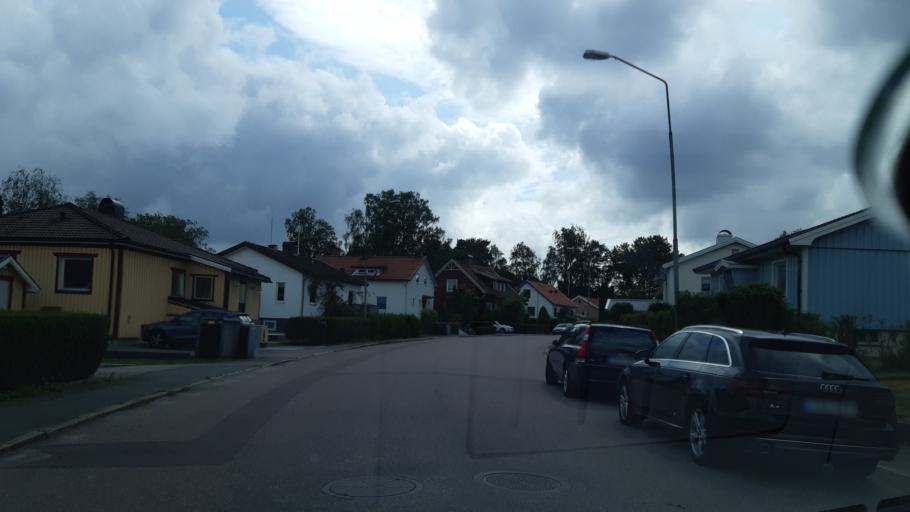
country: SE
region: Vaestra Goetaland
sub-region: Partille Kommun
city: Partille
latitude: 57.7183
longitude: 12.0651
